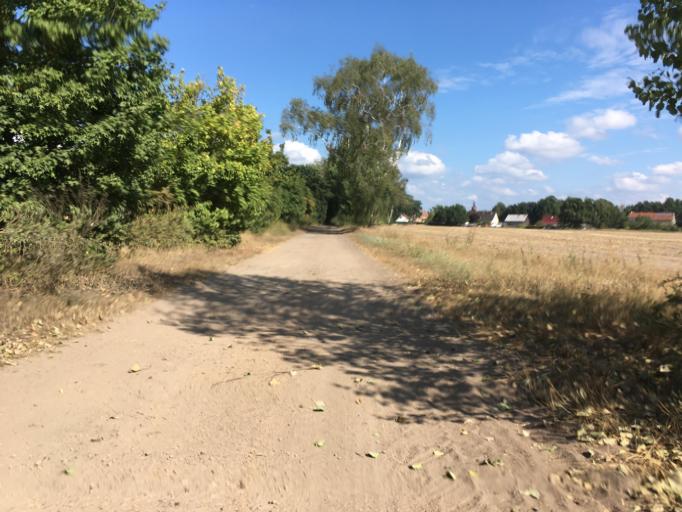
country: DE
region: Brandenburg
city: Zehdenick
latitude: 52.9784
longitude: 13.3808
